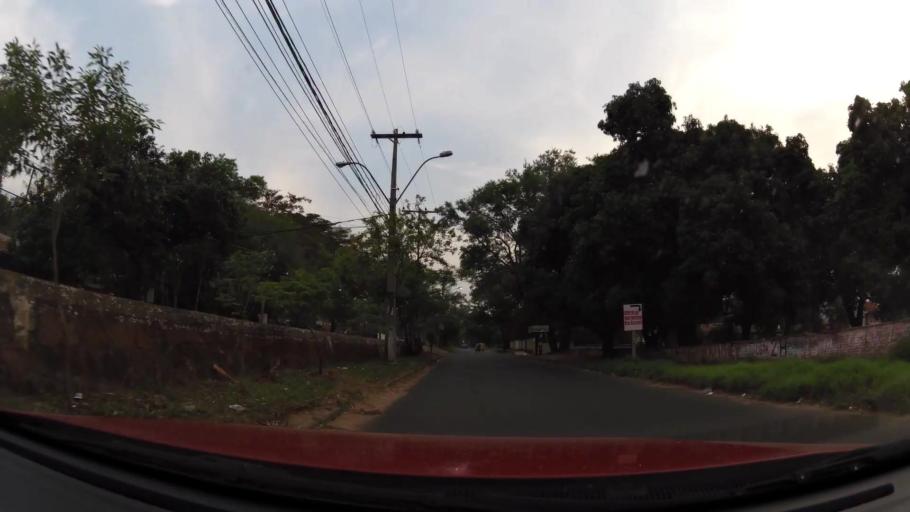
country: PY
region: Central
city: Lambare
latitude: -25.3460
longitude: -57.6391
